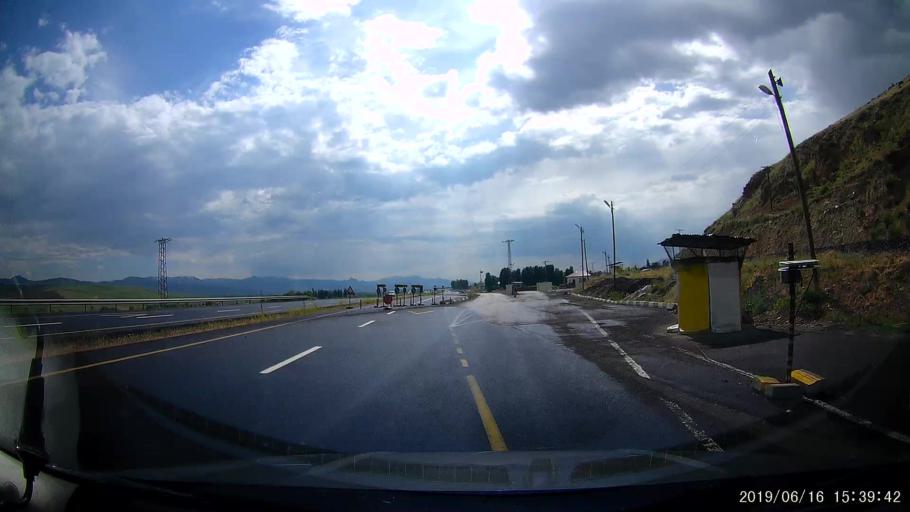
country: TR
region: Erzurum
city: Koprukoy
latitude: 39.9696
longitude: 41.8839
